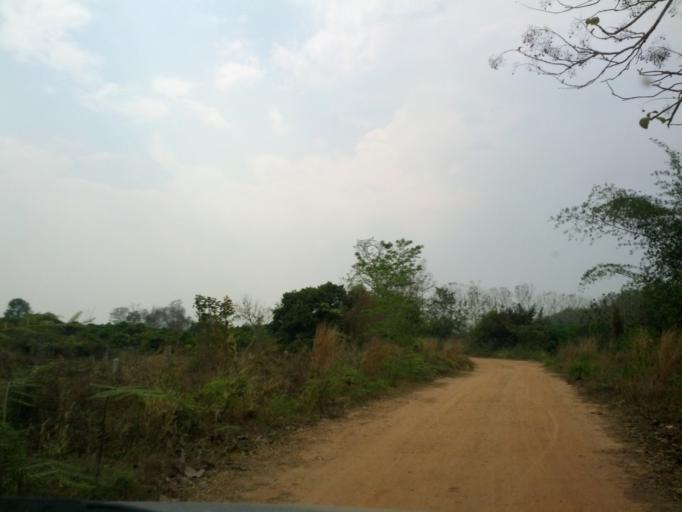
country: TH
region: Chiang Mai
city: Mae Taeng
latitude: 19.1153
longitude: 98.9971
